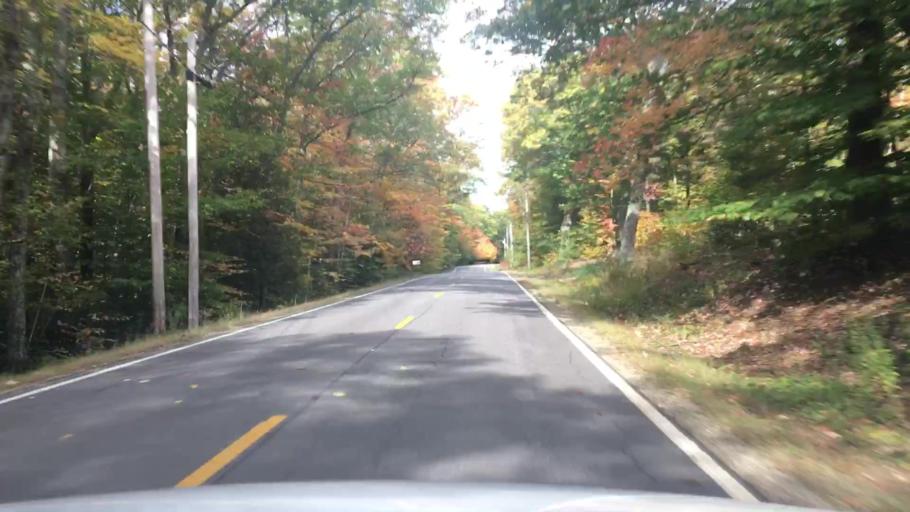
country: US
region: Maine
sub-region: Knox County
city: Hope
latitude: 44.3172
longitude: -69.1234
